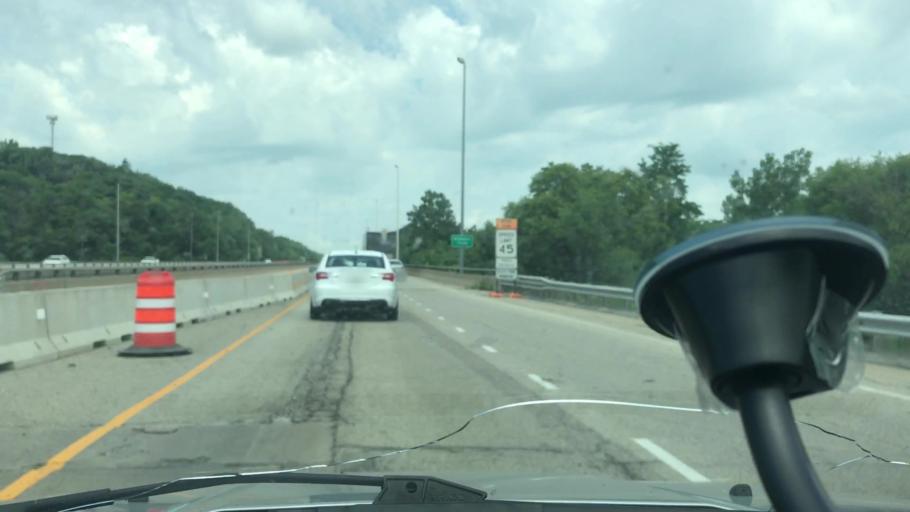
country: US
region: Illinois
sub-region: Peoria County
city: Bartonville
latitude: 40.6602
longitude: -89.6477
